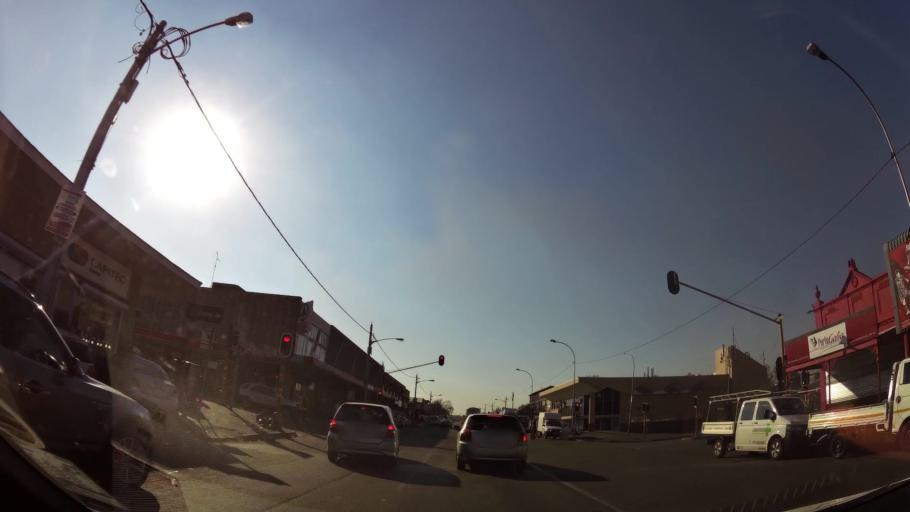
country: ZA
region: Gauteng
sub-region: Ekurhuleni Metropolitan Municipality
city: Germiston
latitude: -26.2014
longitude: 28.1147
